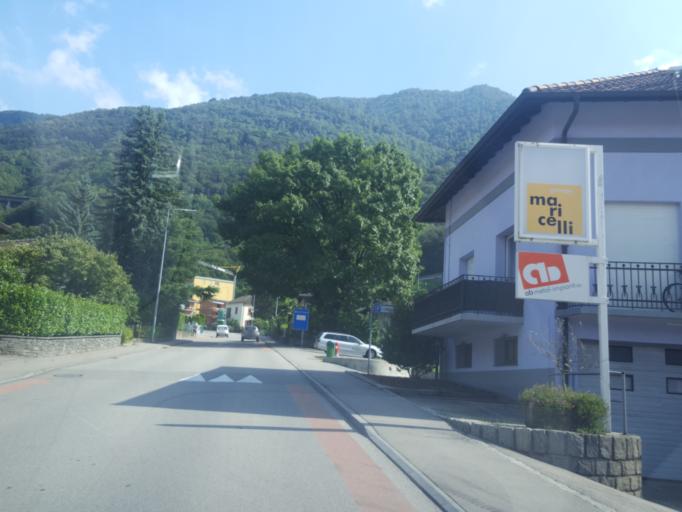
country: CH
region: Ticino
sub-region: Bellinzona District
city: Cadenazzo
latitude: 46.1500
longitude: 8.9488
